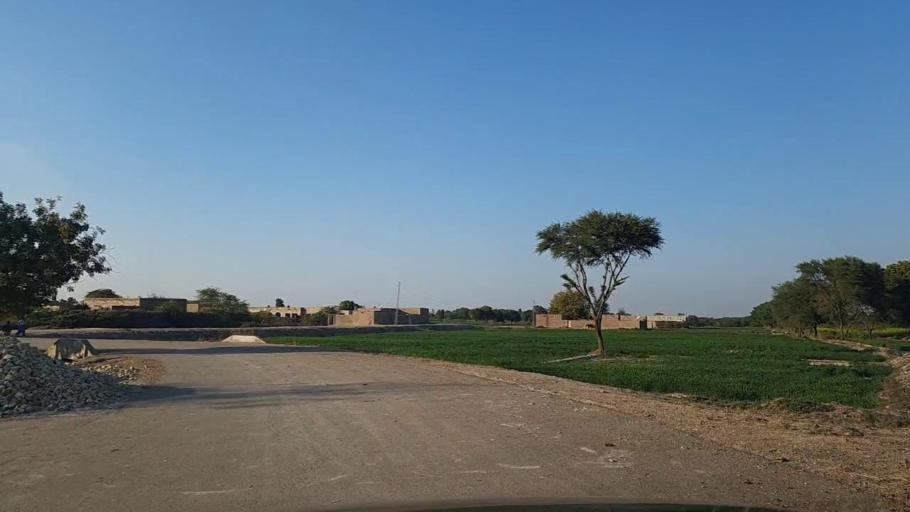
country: PK
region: Sindh
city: Nawabshah
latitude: 26.2286
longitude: 68.3431
